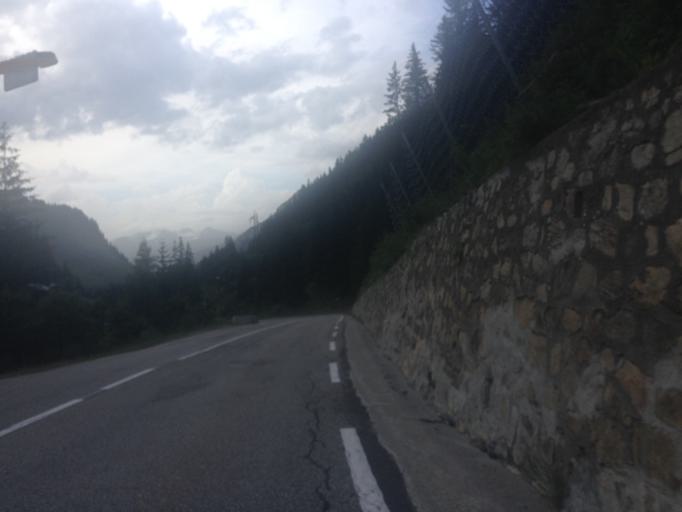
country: FR
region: Rhone-Alpes
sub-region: Departement de la Savoie
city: Tignes
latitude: 45.5161
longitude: 6.9163
